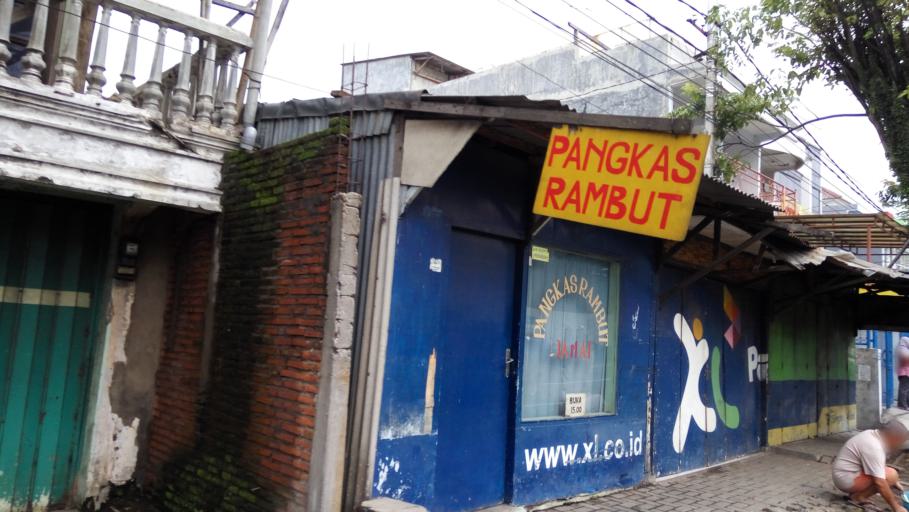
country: ID
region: East Java
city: Malang
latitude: -7.9352
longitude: 112.6047
